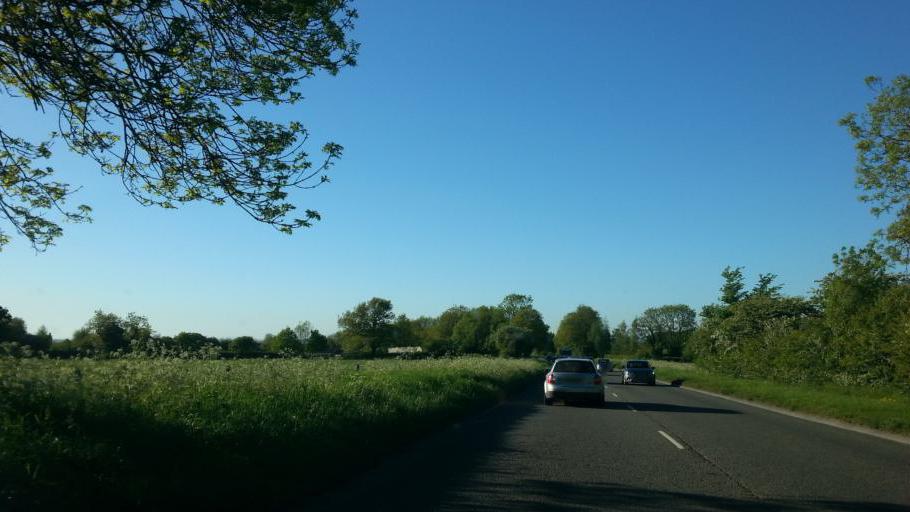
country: GB
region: England
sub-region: Bath and North East Somerset
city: Whitchurch
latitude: 51.3971
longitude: -2.5511
